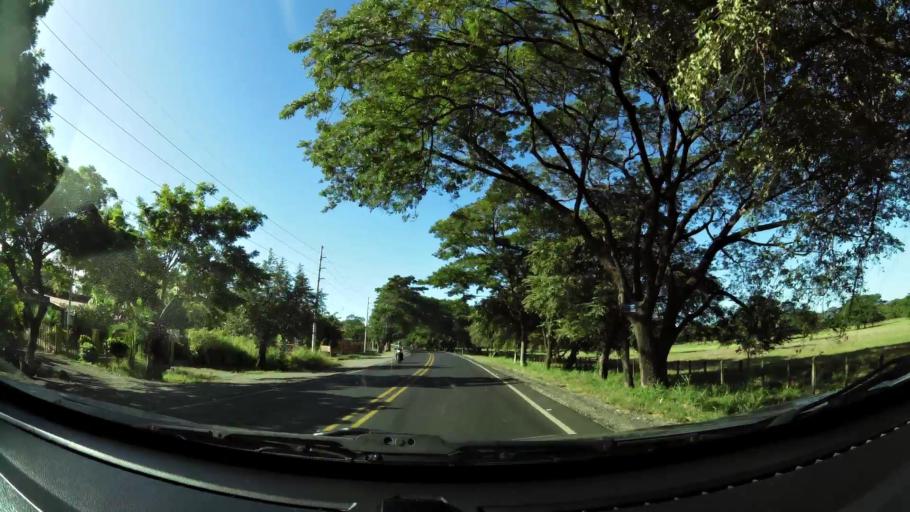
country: CR
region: Guanacaste
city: Belen
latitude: 10.4336
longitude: -85.5666
